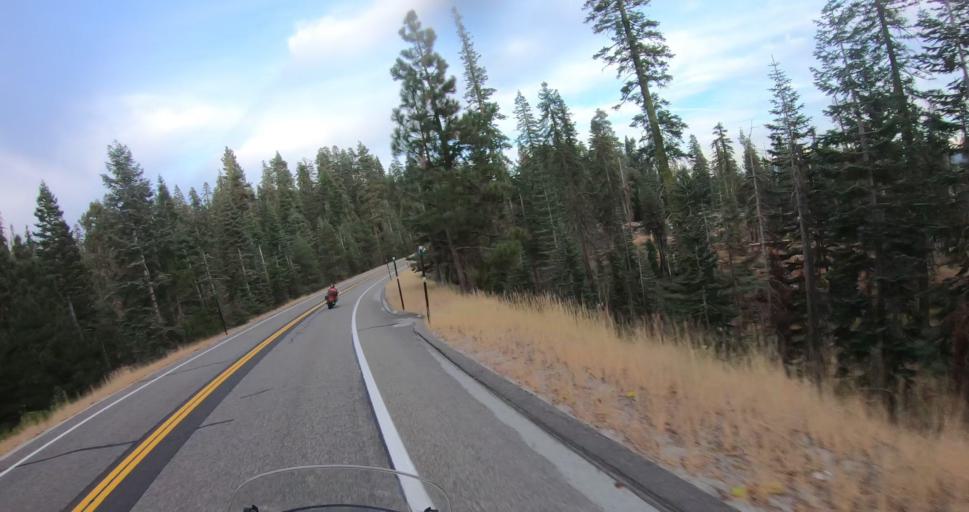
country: US
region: California
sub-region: Calaveras County
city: Arnold
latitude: 38.4093
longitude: -120.1441
